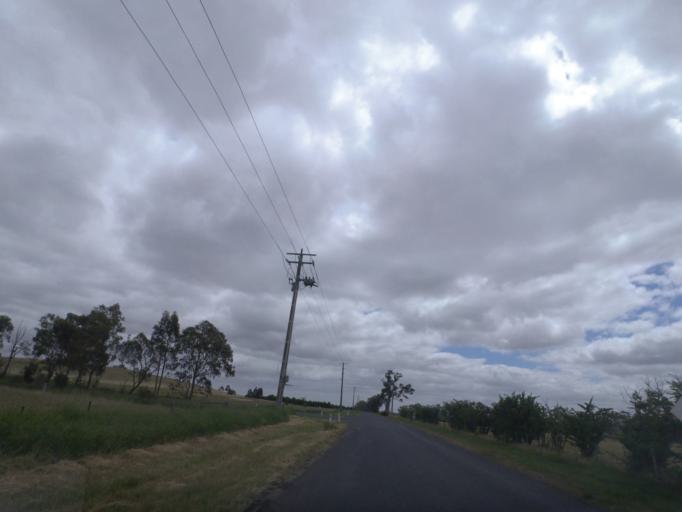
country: AU
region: Victoria
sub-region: Whittlesea
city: Whittlesea
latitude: -37.1864
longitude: 145.0380
